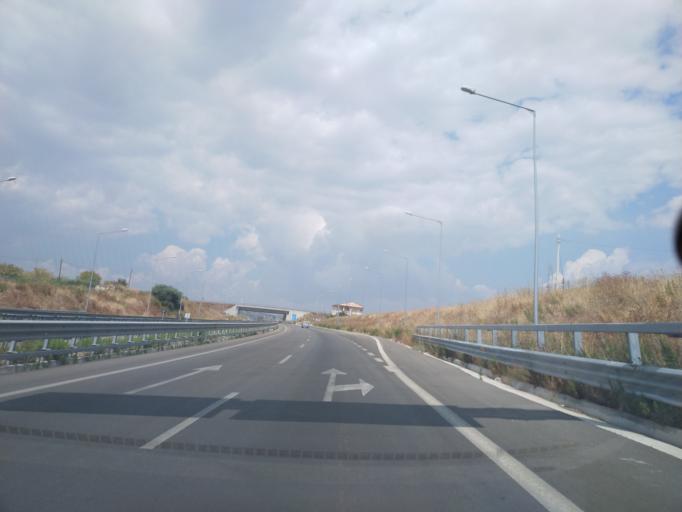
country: IT
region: Sicily
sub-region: Agrigento
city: Favara
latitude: 37.3514
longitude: 13.6785
